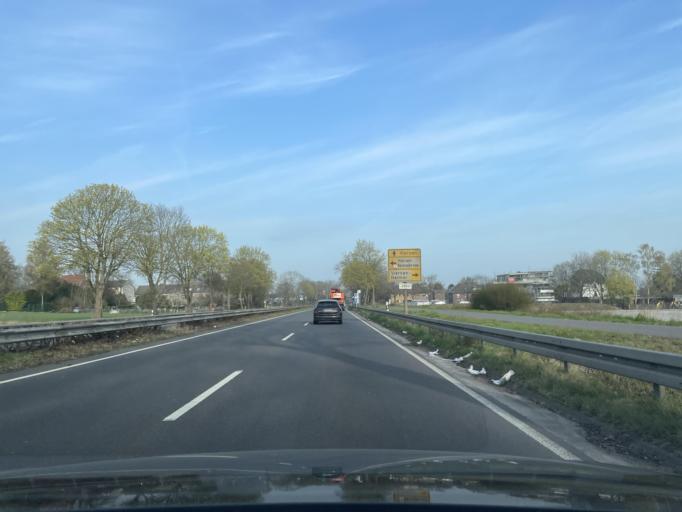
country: DE
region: North Rhine-Westphalia
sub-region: Regierungsbezirk Dusseldorf
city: Viersen
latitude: 51.2284
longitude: 6.4255
